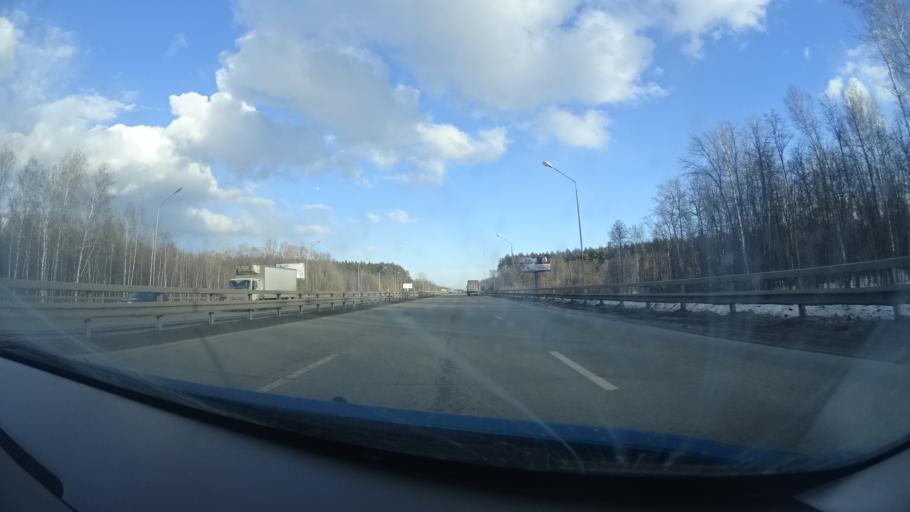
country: RU
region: Bashkortostan
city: Avdon
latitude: 54.6719
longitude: 55.8310
